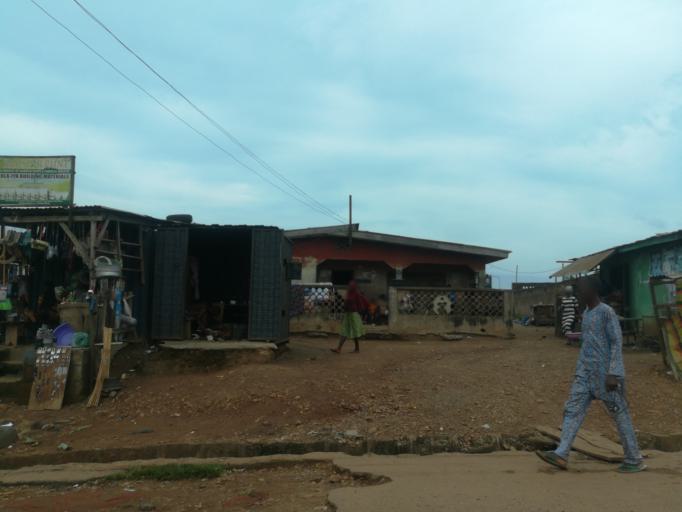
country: NG
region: Oyo
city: Ibadan
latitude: 7.3745
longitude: 3.9618
